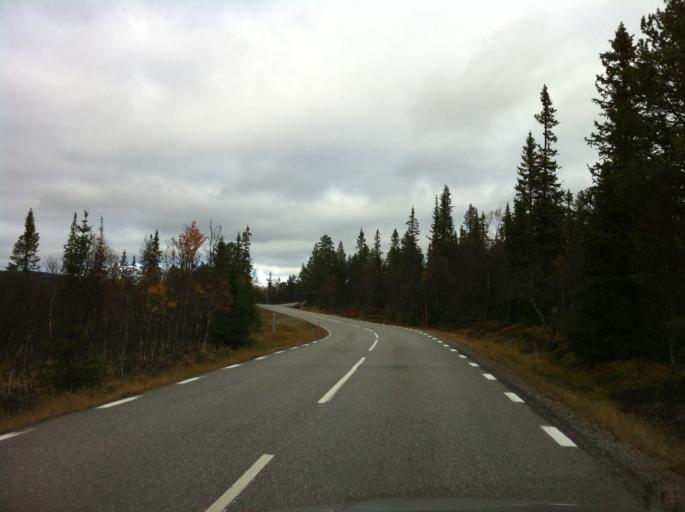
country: NO
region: Hedmark
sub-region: Engerdal
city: Engerdal
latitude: 62.0850
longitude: 12.3097
